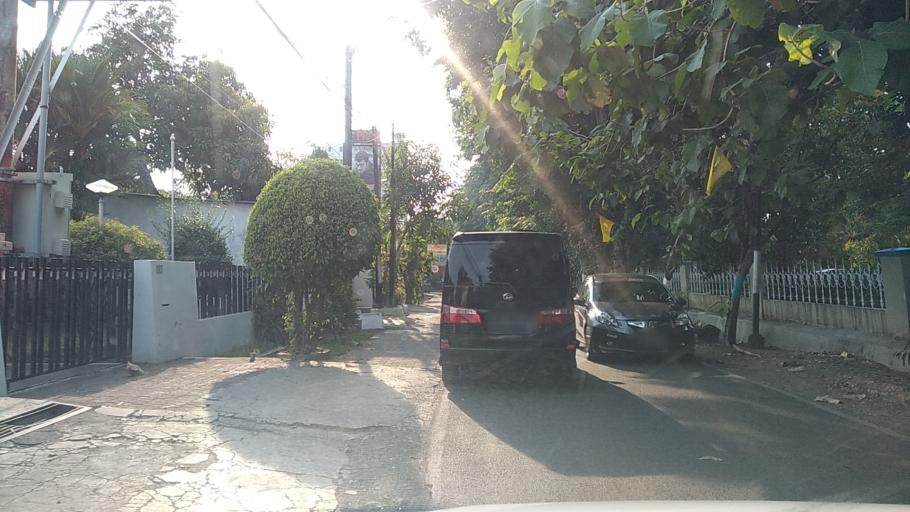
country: ID
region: Central Java
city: Semarang
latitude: -7.0003
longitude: 110.4293
